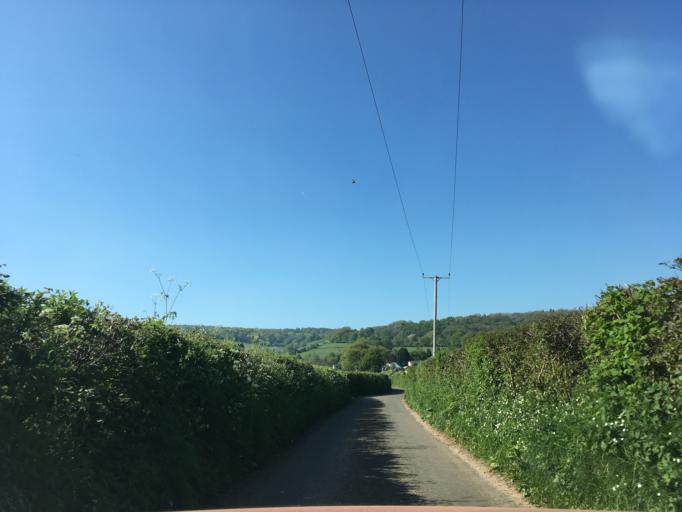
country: GB
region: Wales
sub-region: Newport
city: Llanvaches
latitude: 51.6223
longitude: -2.7965
